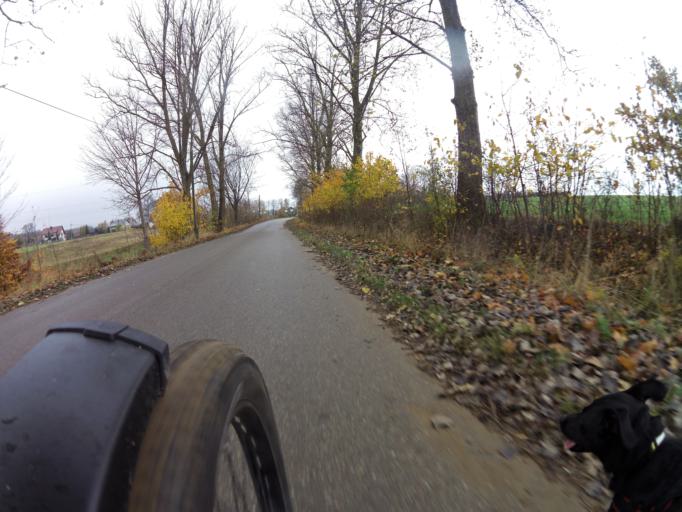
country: PL
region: Pomeranian Voivodeship
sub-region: Powiat pucki
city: Krokowa
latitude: 54.7214
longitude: 18.1380
